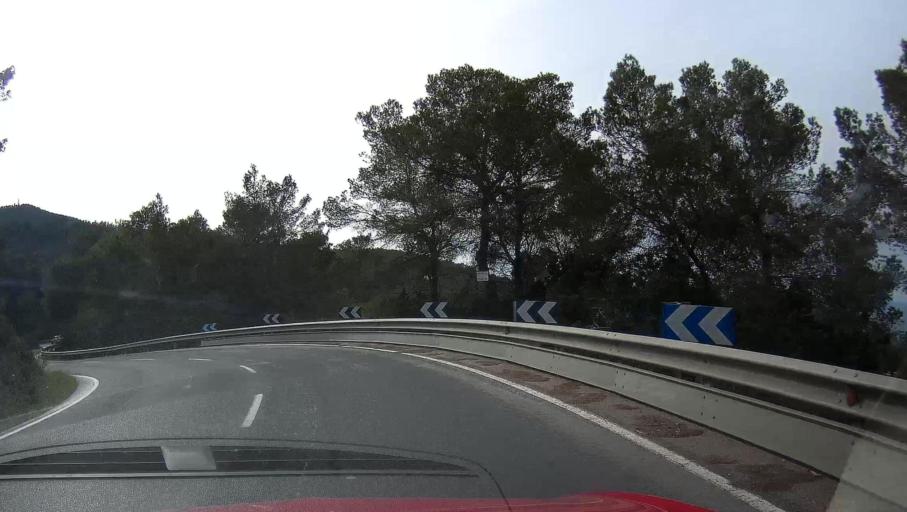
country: ES
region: Balearic Islands
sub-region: Illes Balears
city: Sant Joan de Labritja
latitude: 39.0803
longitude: 1.5021
